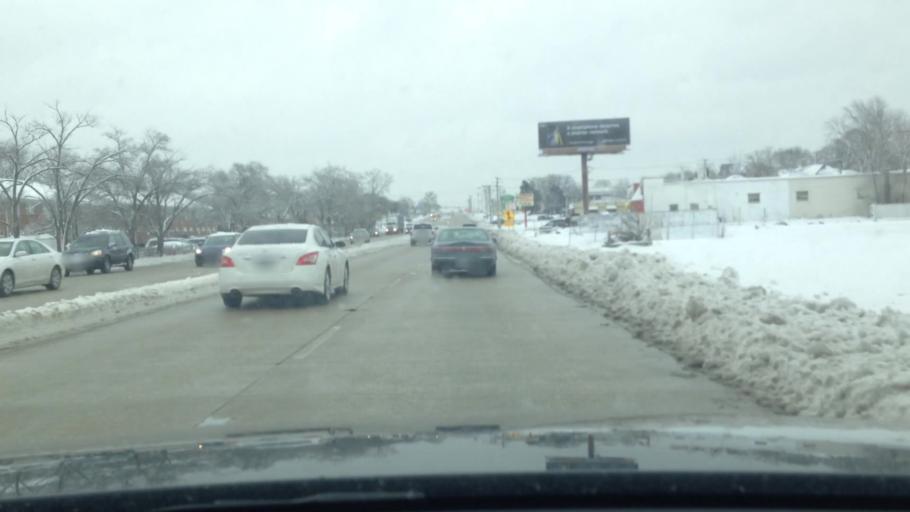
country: US
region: Illinois
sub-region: DuPage County
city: Glen Ellyn
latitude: 41.8596
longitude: -88.0368
